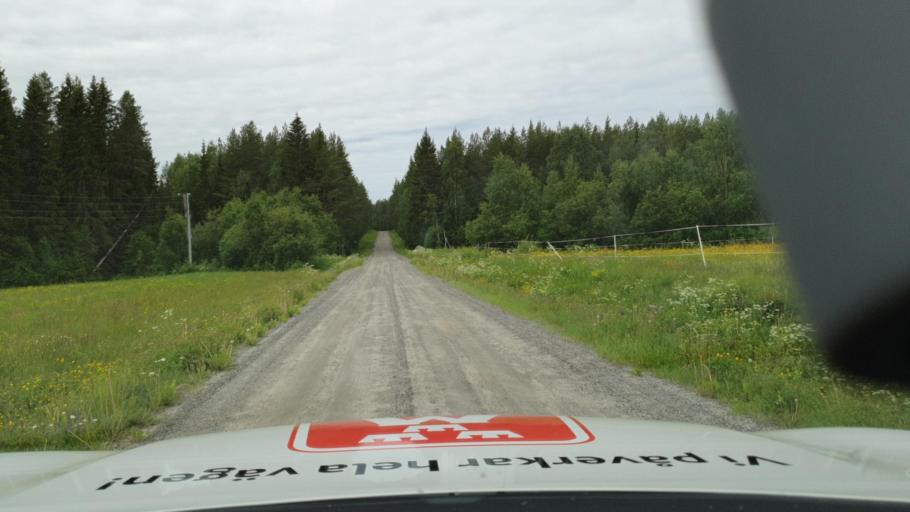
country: SE
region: Vaesterbotten
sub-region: Skelleftea Kommun
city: Burtraesk
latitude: 64.4468
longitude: 20.3297
